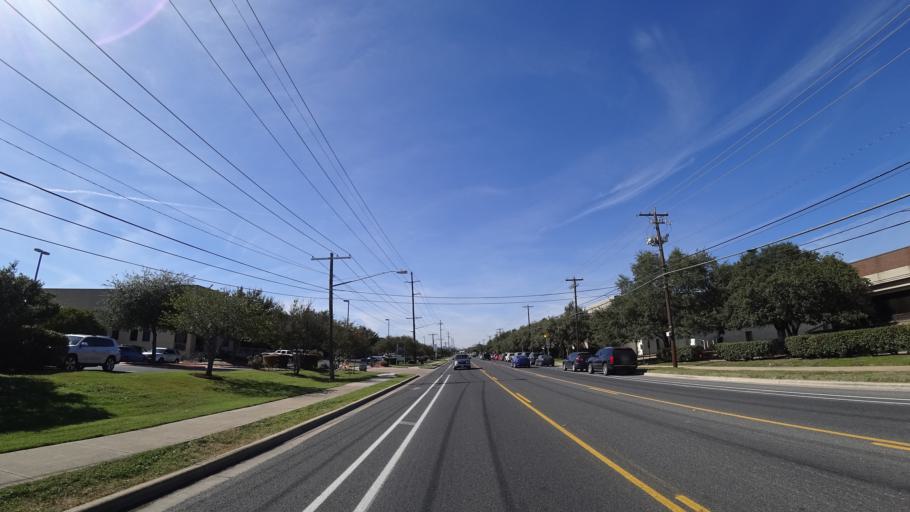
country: US
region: Texas
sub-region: Travis County
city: Austin
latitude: 30.2090
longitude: -97.7450
